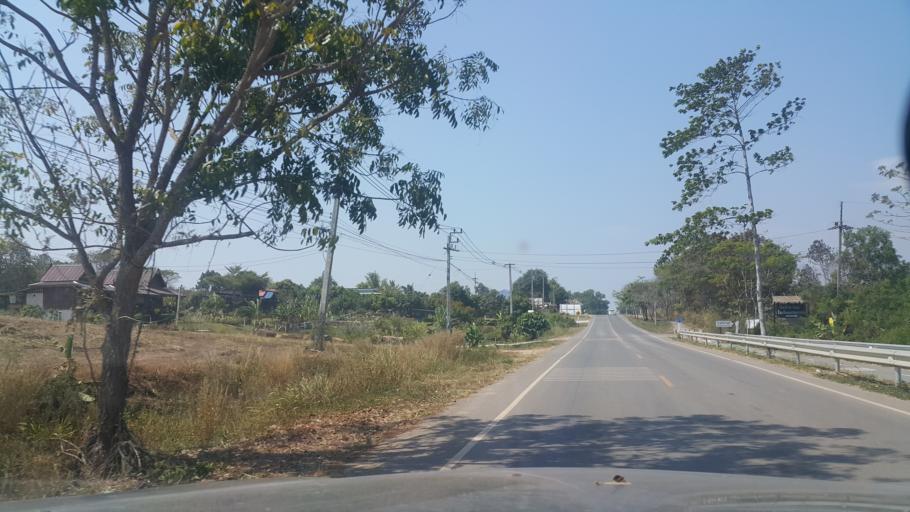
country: TH
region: Nakhon Ratchasima
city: Wang Nam Khiao
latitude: 14.3550
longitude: 101.9281
